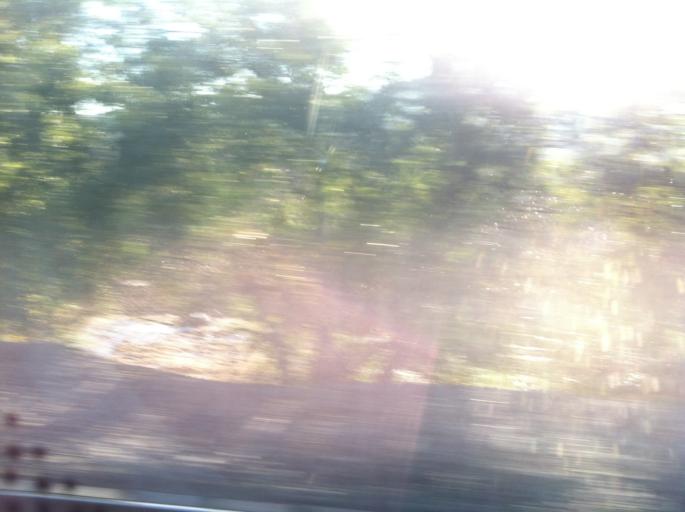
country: ES
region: Castille and Leon
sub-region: Provincia de Valladolid
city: Cabezon
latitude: 41.7173
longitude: -4.6649
